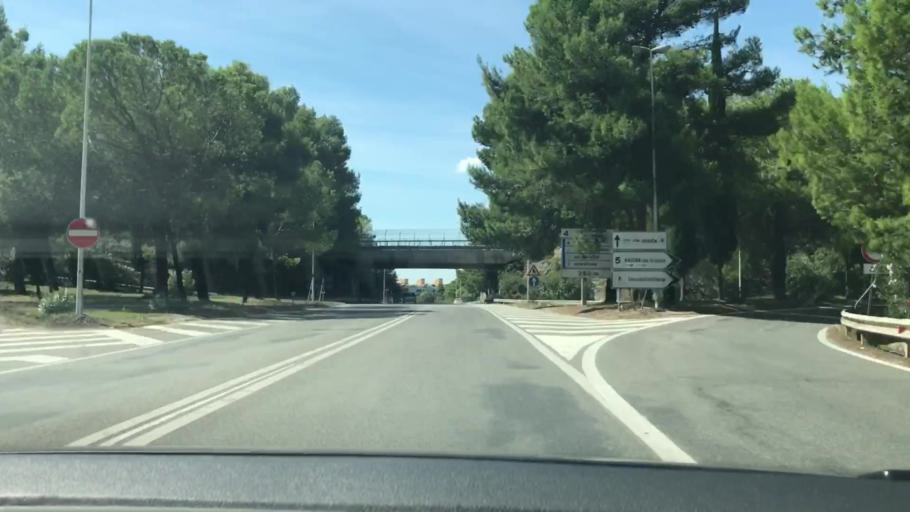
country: IT
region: Basilicate
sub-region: Provincia di Matera
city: Matera
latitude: 40.6805
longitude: 16.5871
